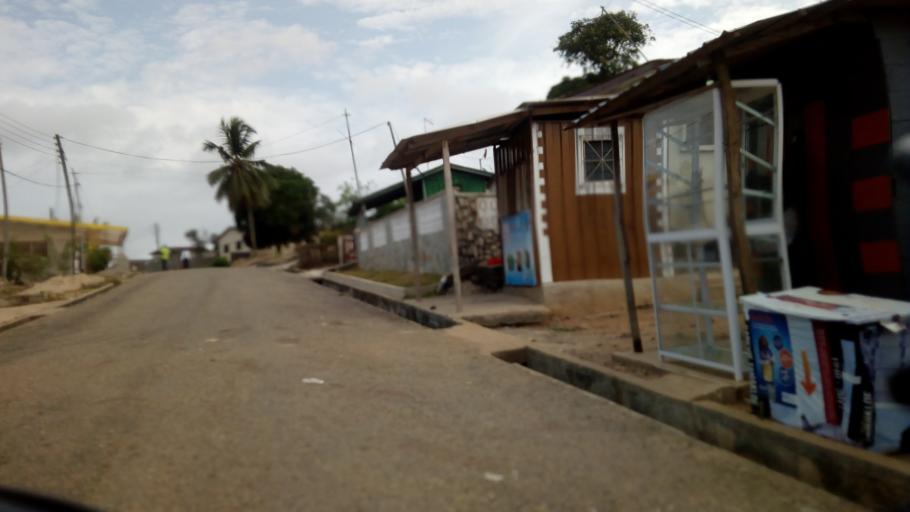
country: GH
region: Central
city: Cape Coast
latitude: 5.1035
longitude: -1.2776
